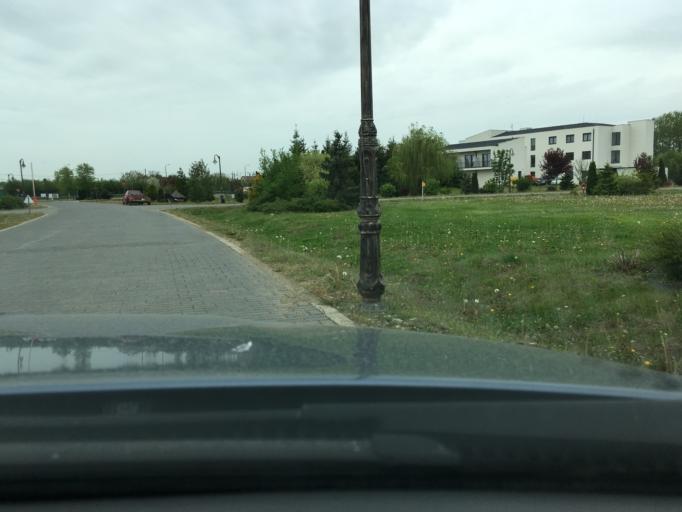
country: HU
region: Hajdu-Bihar
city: Debrecen
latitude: 47.5497
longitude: 21.6889
